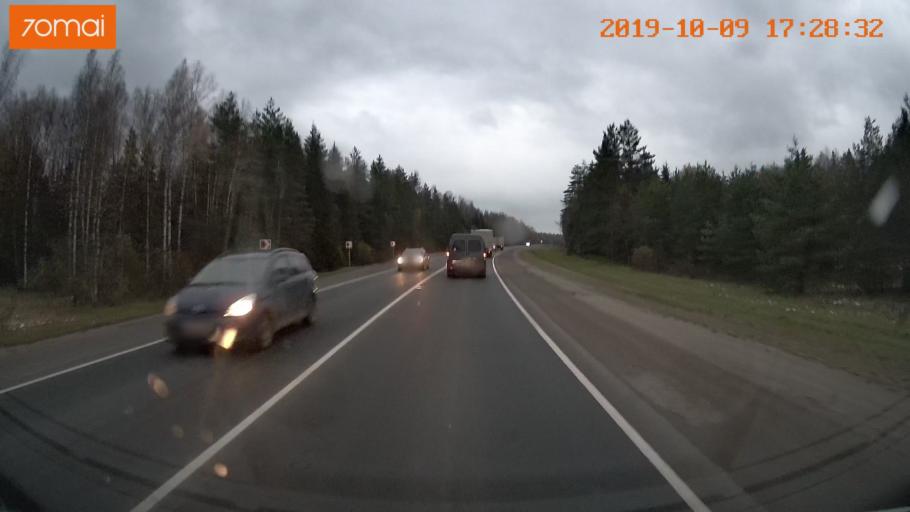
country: RU
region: Ivanovo
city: Furmanov
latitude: 57.1571
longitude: 41.0678
